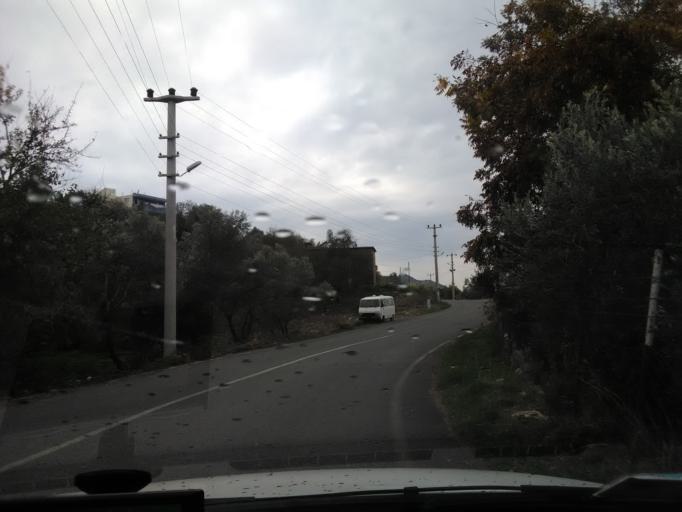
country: TR
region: Antalya
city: Gazipasa
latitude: 36.2589
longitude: 32.3141
